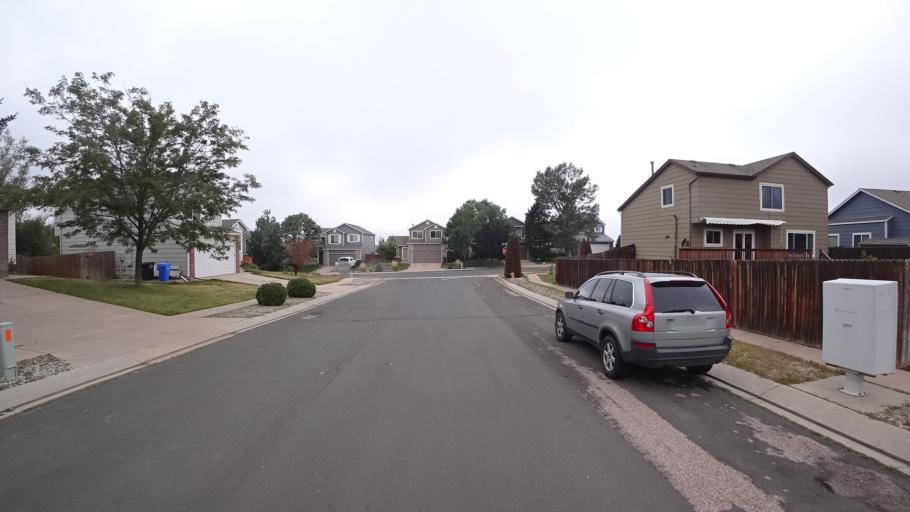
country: US
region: Colorado
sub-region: El Paso County
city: Black Forest
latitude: 38.9367
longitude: -104.7434
